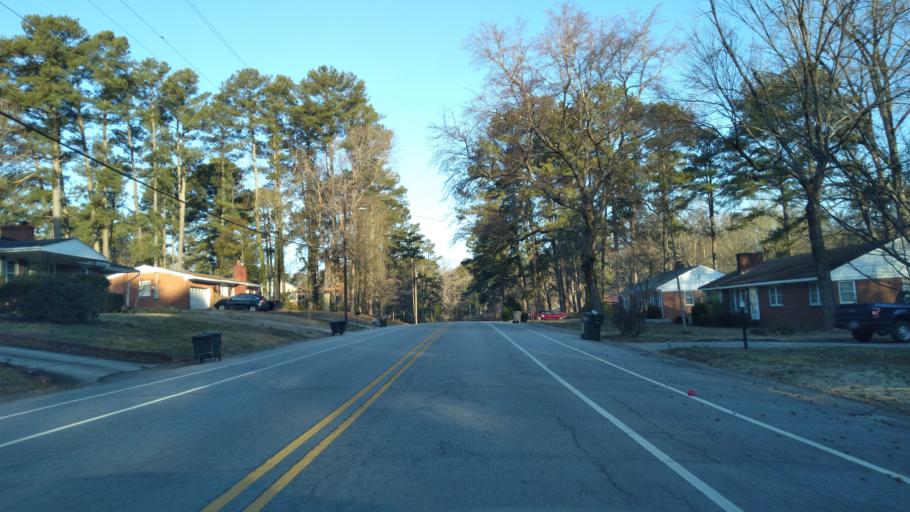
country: US
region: North Carolina
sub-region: Wake County
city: Garner
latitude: 35.7000
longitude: -78.6232
